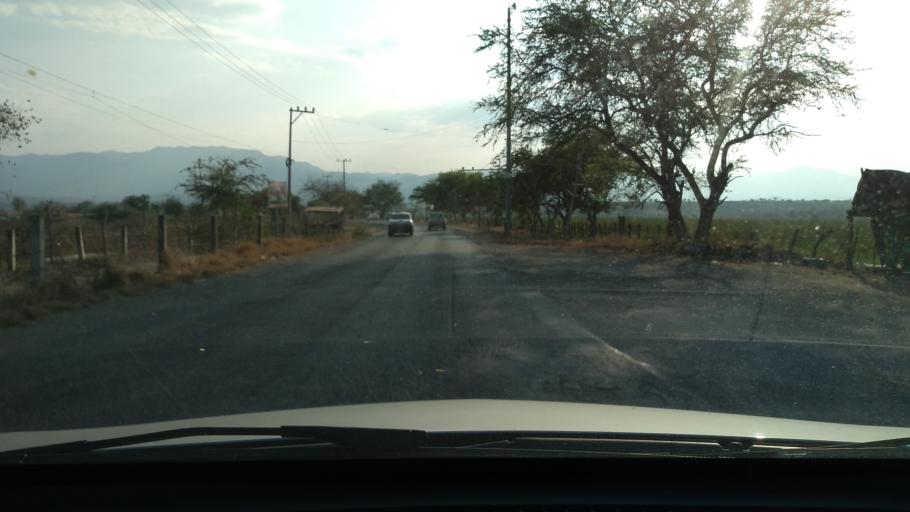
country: MX
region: Morelos
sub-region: Jojutla
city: Tehuixtla
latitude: 18.5869
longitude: -99.2620
